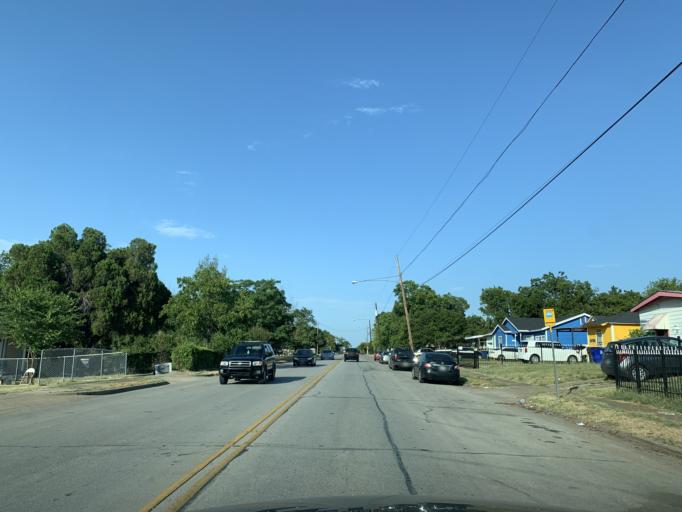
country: US
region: Texas
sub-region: Dallas County
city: Dallas
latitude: 32.7093
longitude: -96.7891
